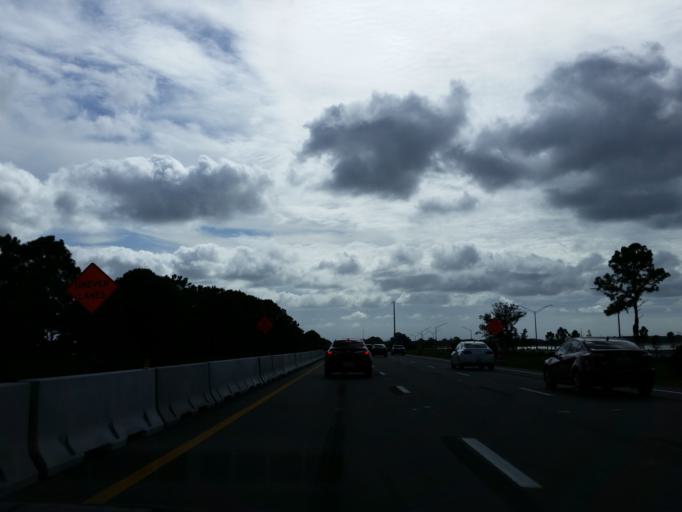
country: US
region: Florida
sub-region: Sarasota County
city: The Meadows
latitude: 27.3743
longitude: -82.4468
